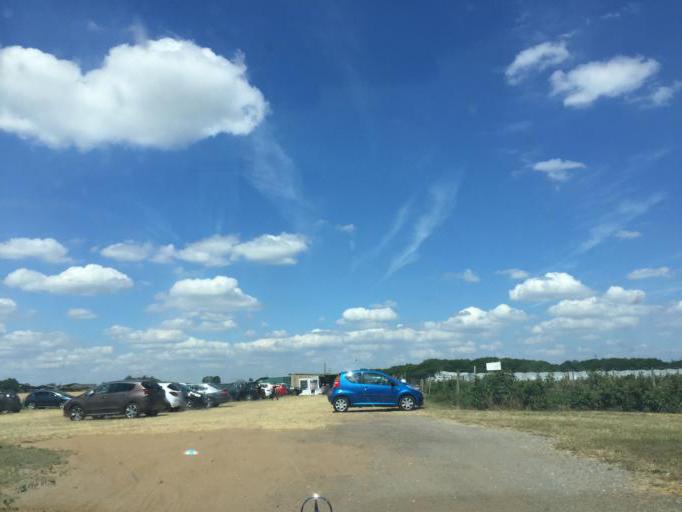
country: GB
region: England
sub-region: Leicestershire
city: Hinckley
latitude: 52.4921
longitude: -1.3363
